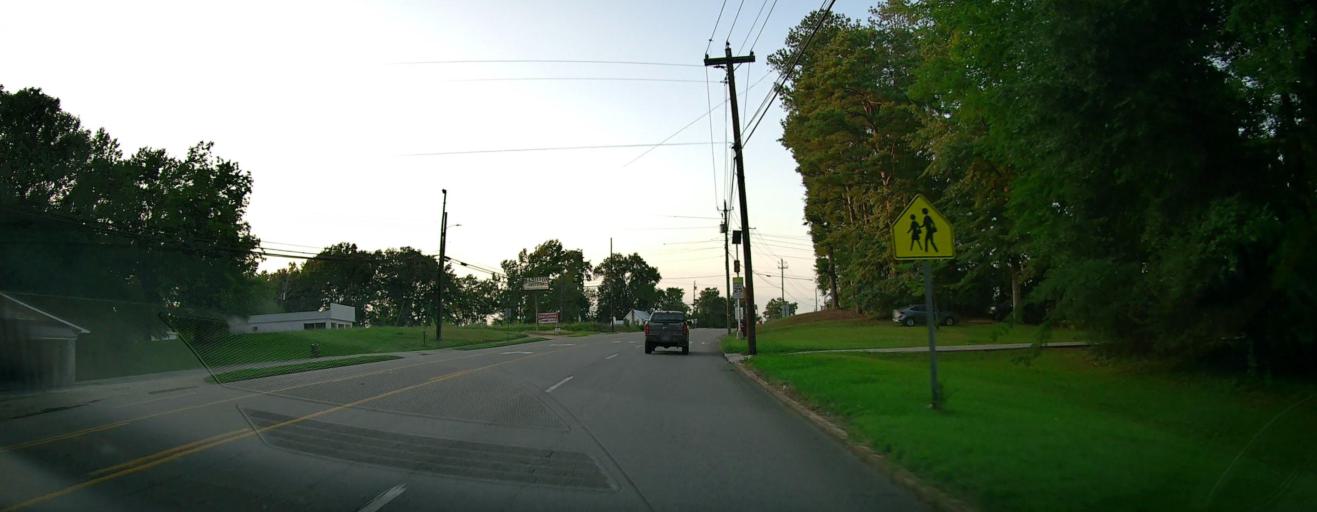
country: US
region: Alabama
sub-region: Marion County
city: Hamilton
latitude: 34.1351
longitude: -87.9904
